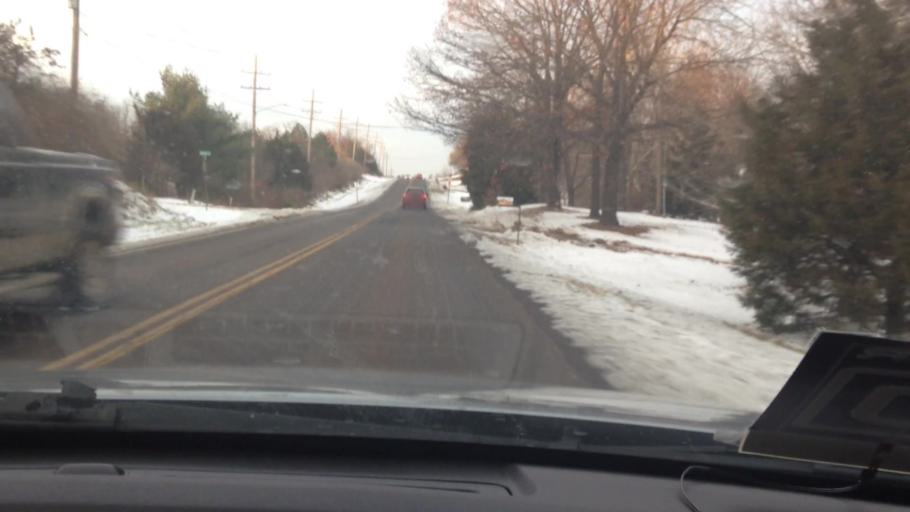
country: US
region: Kansas
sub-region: Leavenworth County
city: Lansing
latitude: 39.2405
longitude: -94.9190
